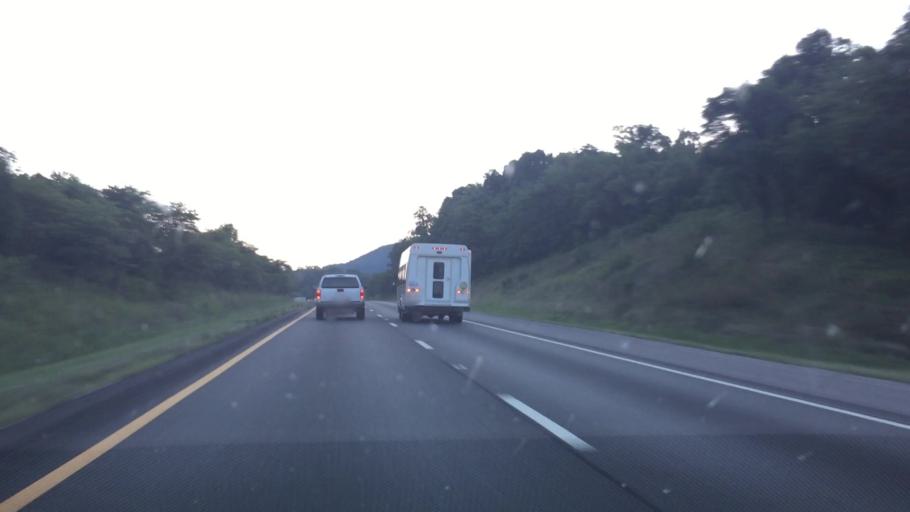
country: US
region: Virginia
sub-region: Montgomery County
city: Shawsville
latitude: 37.2501
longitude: -80.1976
